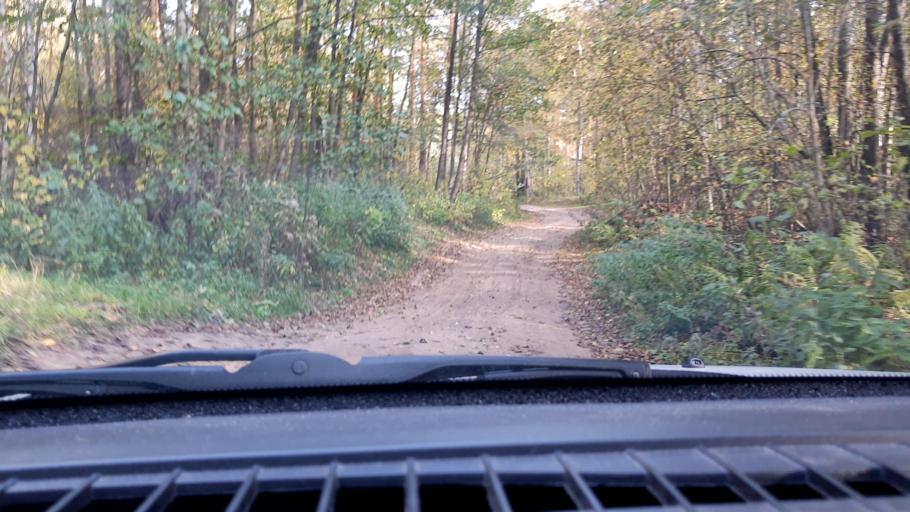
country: RU
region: Nizjnij Novgorod
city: Lukino
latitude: 56.3929
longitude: 43.6267
